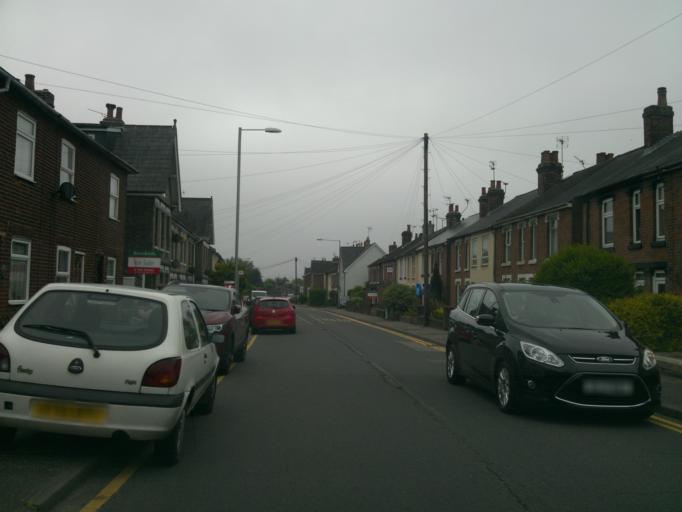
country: GB
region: England
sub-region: Essex
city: Colchester
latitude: 51.9035
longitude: 0.8901
